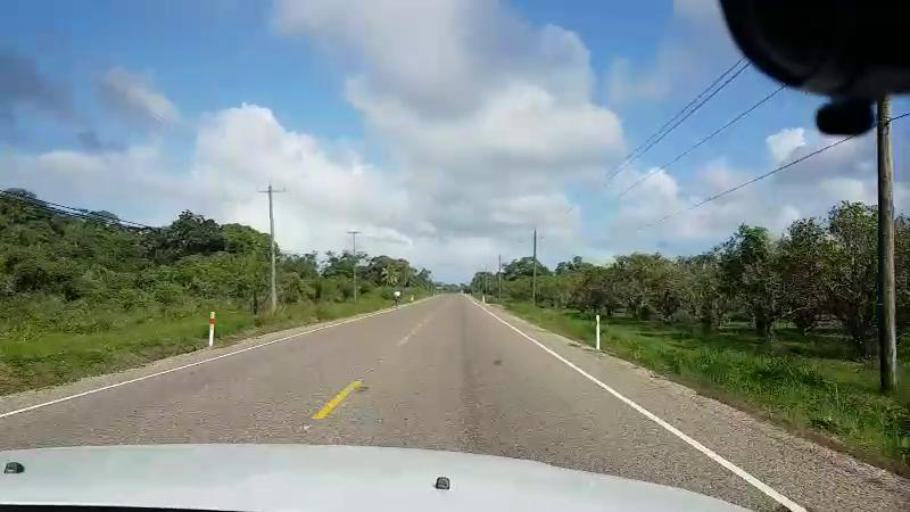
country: BZ
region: Stann Creek
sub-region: Dangriga
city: Dangriga
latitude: 16.9955
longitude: -88.3580
